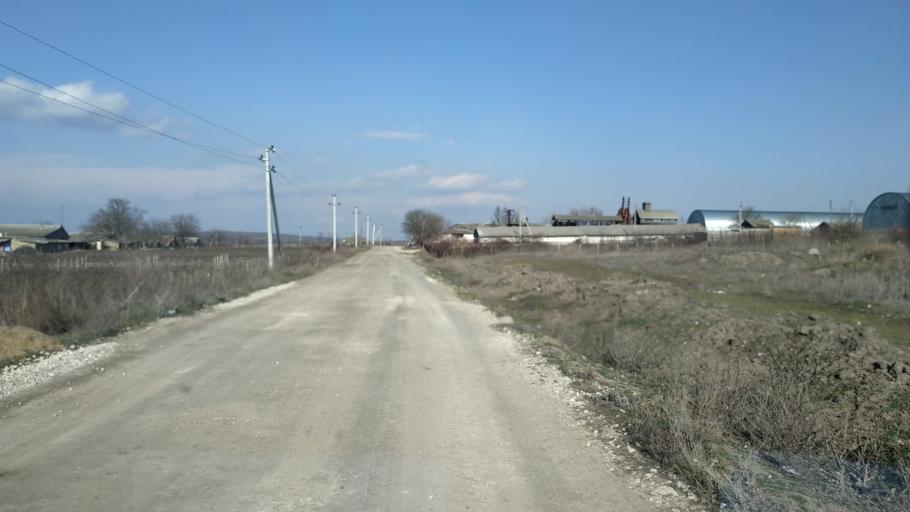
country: MD
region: Basarabeasca
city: Basarabeasca
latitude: 46.5734
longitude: 29.1228
